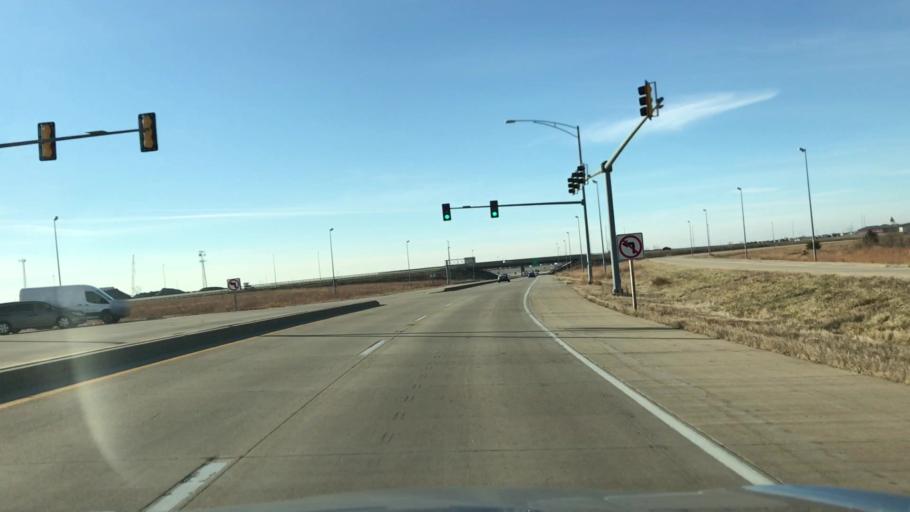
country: US
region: Illinois
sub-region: McLean County
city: Normal
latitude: 40.5409
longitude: -88.9452
